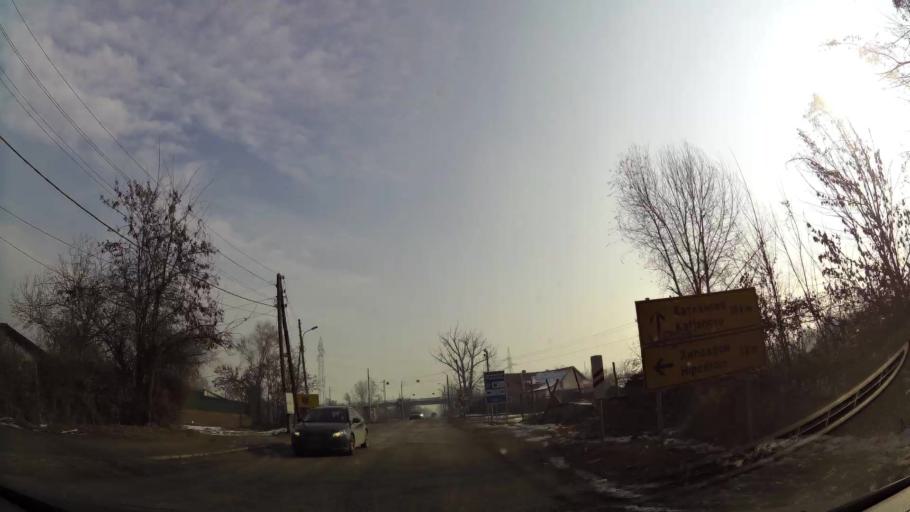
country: MK
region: Kisela Voda
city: Kisela Voda
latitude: 41.9914
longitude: 21.5095
